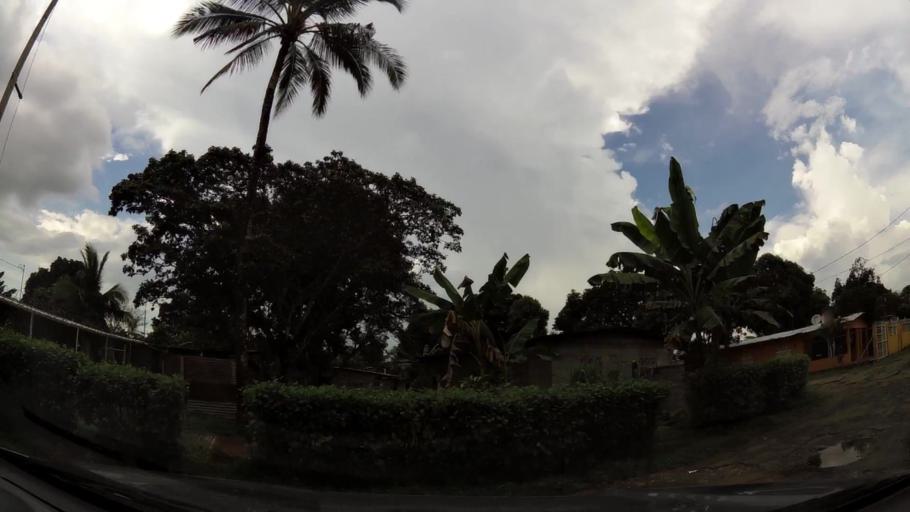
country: PA
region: Panama
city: Cabra Numero Uno
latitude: 9.1078
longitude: -79.3247
